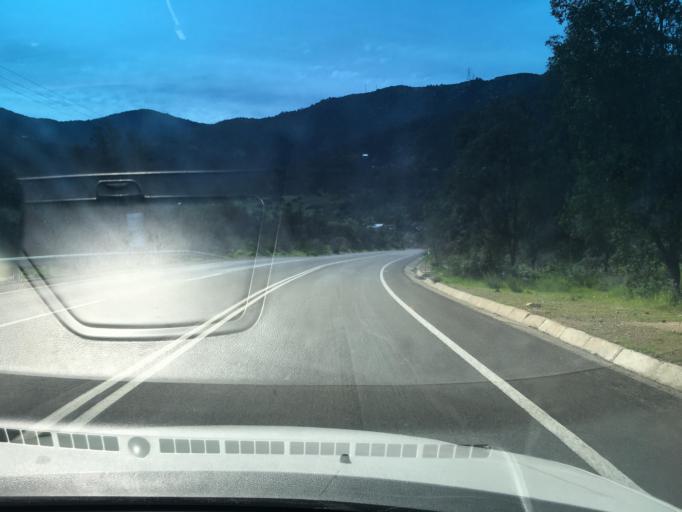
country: CL
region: Valparaiso
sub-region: Provincia de San Felipe
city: Llaillay
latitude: -33.0616
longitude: -71.0289
